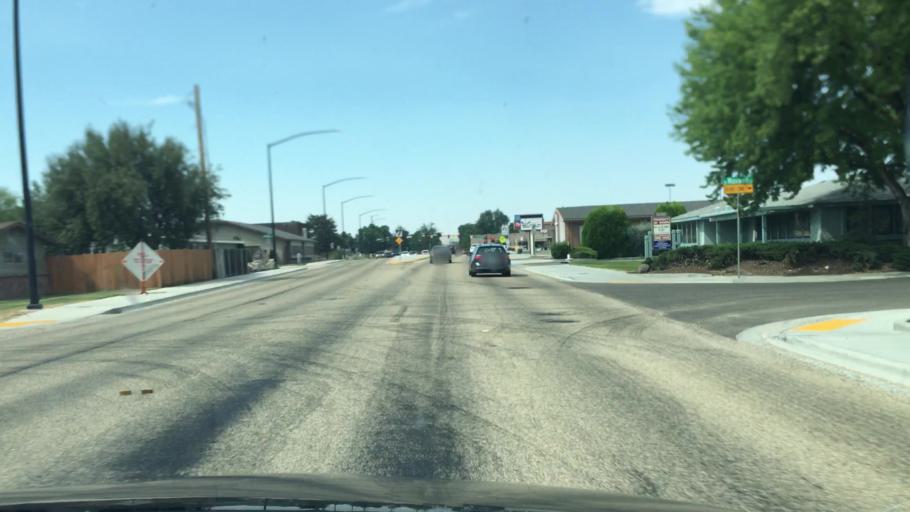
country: US
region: Idaho
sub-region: Ada County
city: Garden City
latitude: 43.6168
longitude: -116.2742
